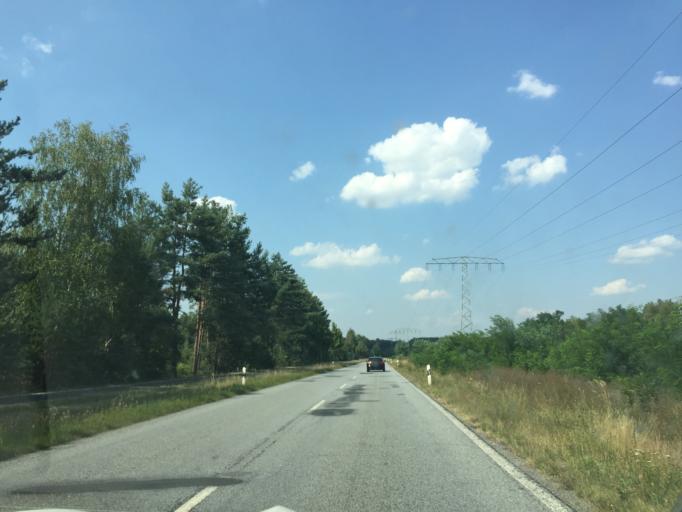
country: DE
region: Saxony
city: Boxberg
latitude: 51.4274
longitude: 14.5361
